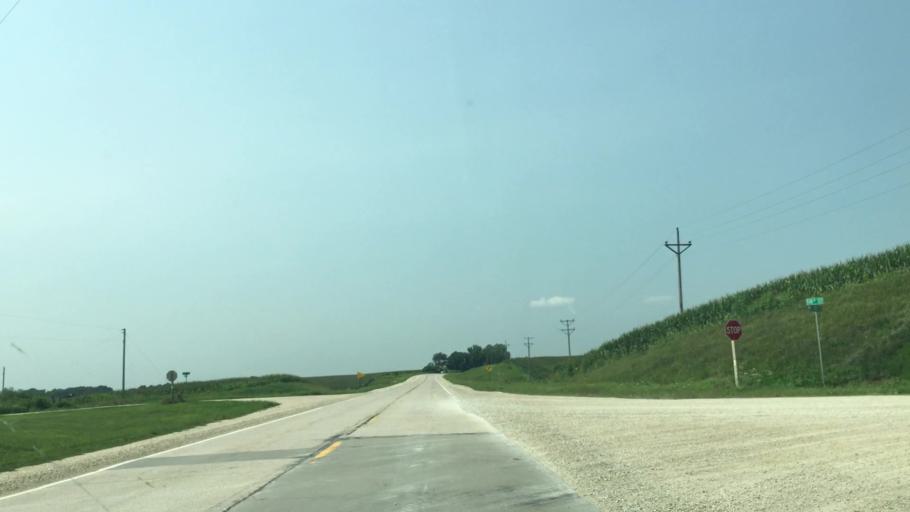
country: US
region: Iowa
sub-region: Fayette County
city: West Union
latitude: 43.0965
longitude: -91.8634
